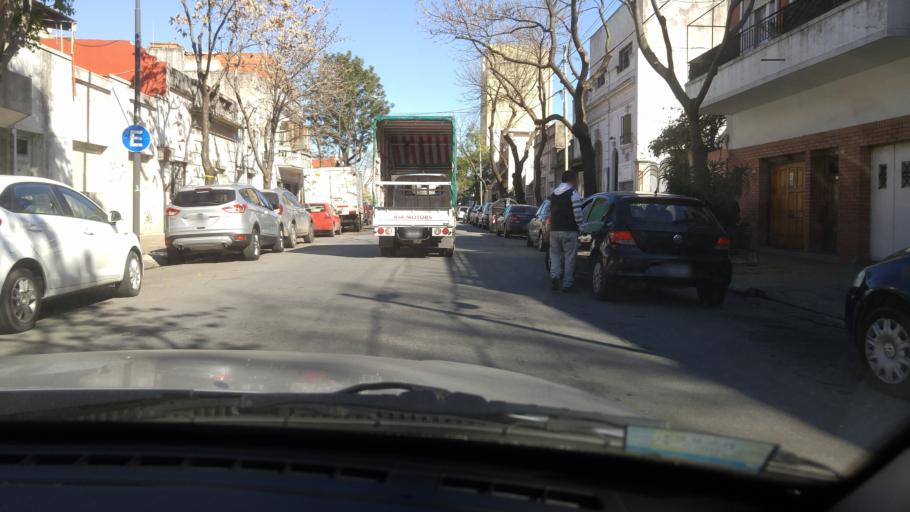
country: AR
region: Buenos Aires F.D.
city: Villa Santa Rita
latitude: -34.6183
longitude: -58.4781
